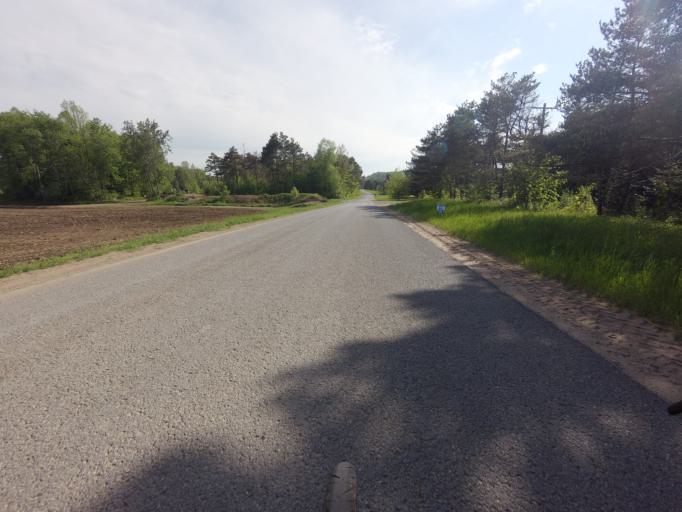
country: US
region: New York
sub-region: St. Lawrence County
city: Gouverneur
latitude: 44.2261
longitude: -75.2317
